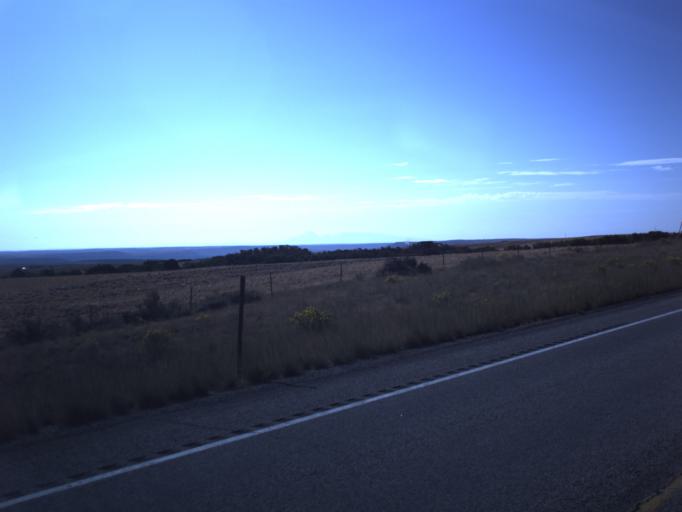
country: US
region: Utah
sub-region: San Juan County
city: Monticello
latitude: 37.8413
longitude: -109.3369
